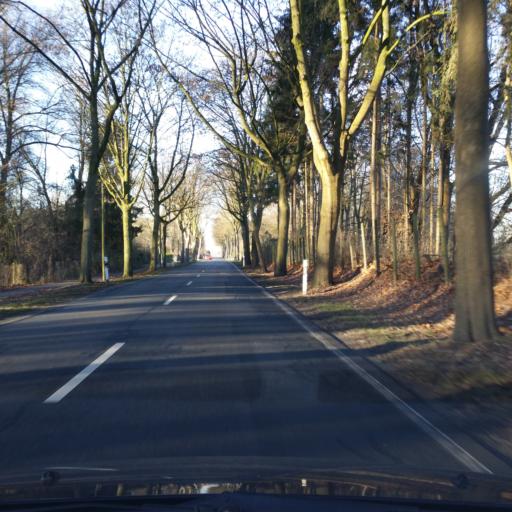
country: DE
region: North Rhine-Westphalia
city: Kalkar
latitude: 51.7329
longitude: 6.3388
